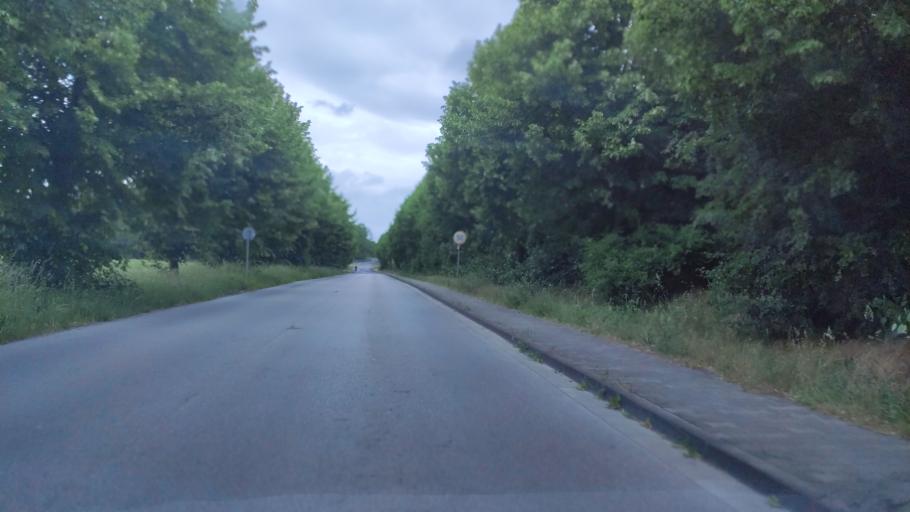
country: DE
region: North Rhine-Westphalia
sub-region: Regierungsbezirk Dusseldorf
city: Neubrueck
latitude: 51.1658
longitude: 6.6580
